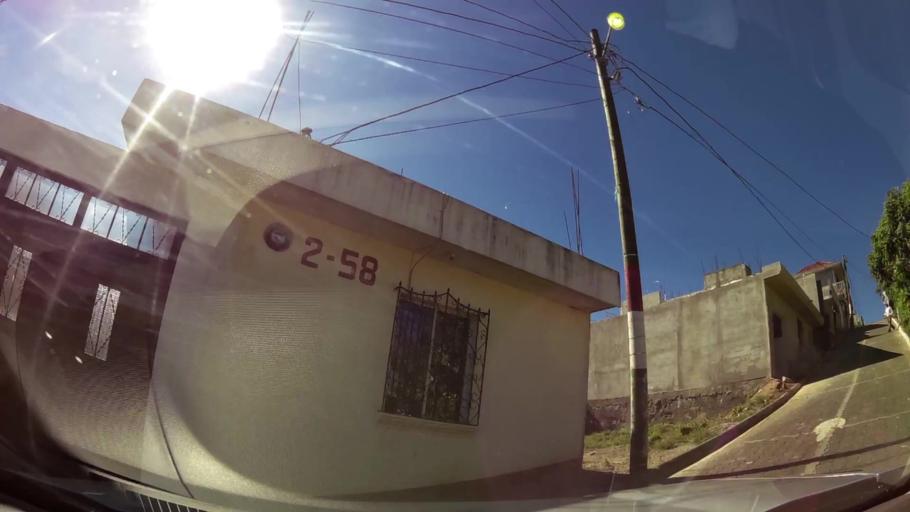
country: GT
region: Guatemala
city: Fraijanes
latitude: 14.4635
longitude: -90.4365
